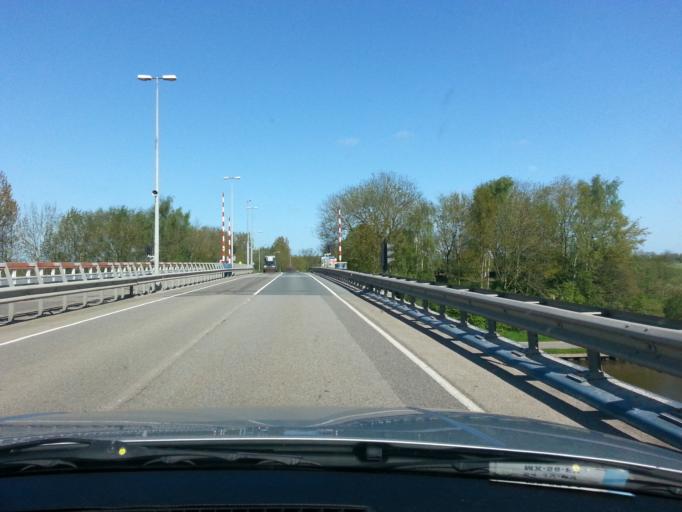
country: NL
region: Friesland
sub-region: Gemeente Achtkarspelen
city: Augustinusga
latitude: 53.2261
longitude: 6.1740
